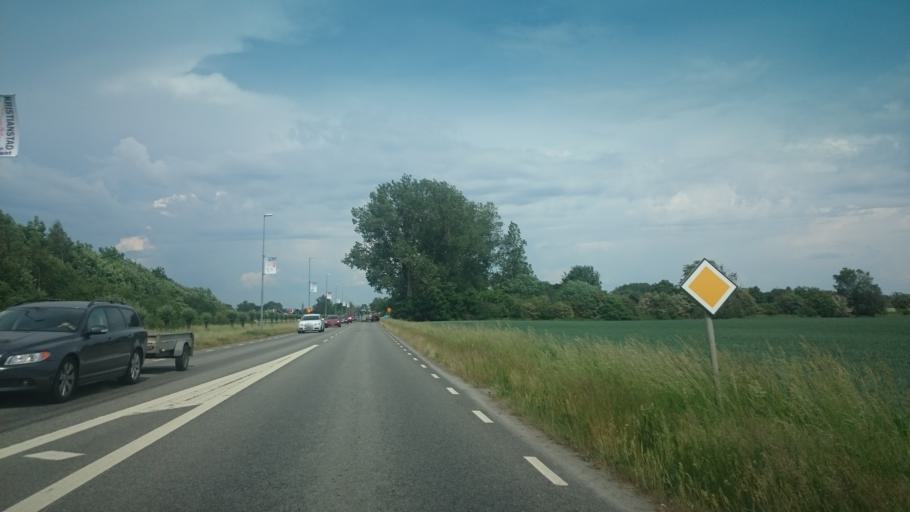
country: SE
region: Skane
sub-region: Kristianstads Kommun
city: Norra Asum
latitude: 56.0038
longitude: 14.1511
